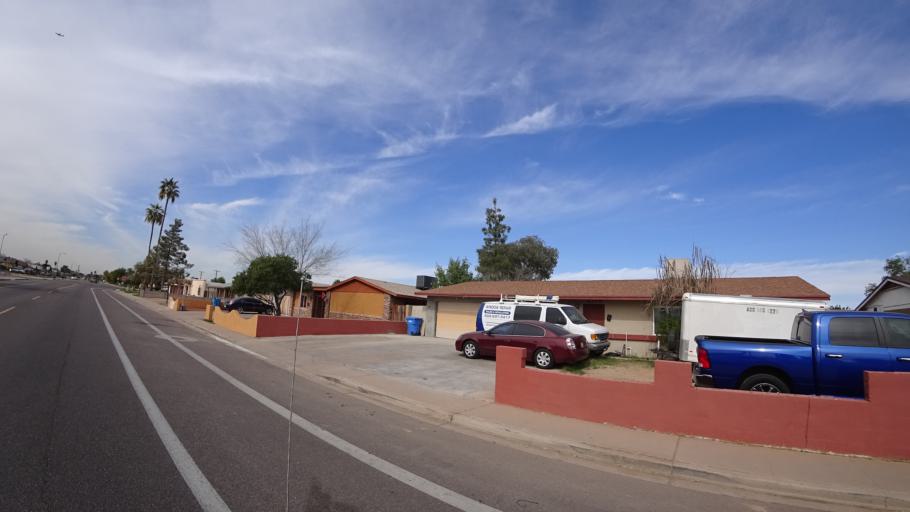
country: US
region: Arizona
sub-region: Maricopa County
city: Glendale
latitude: 33.4877
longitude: -112.1938
